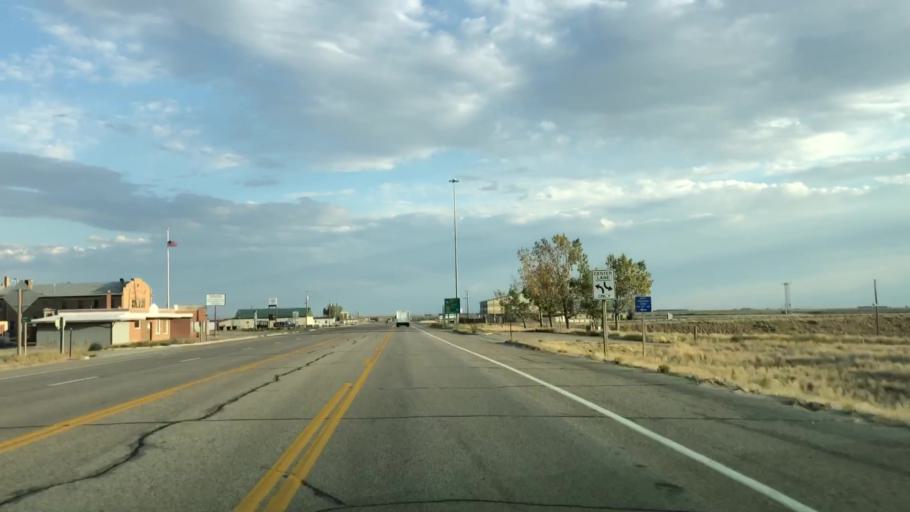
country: US
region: Wyoming
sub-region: Sweetwater County
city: North Rock Springs
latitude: 42.1103
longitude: -109.4496
